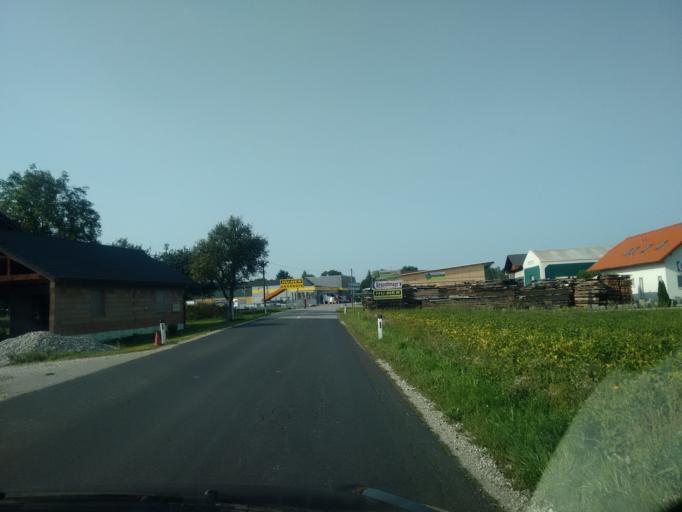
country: AT
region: Upper Austria
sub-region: Wels-Land
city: Gunskirchen
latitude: 48.1566
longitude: 13.9606
